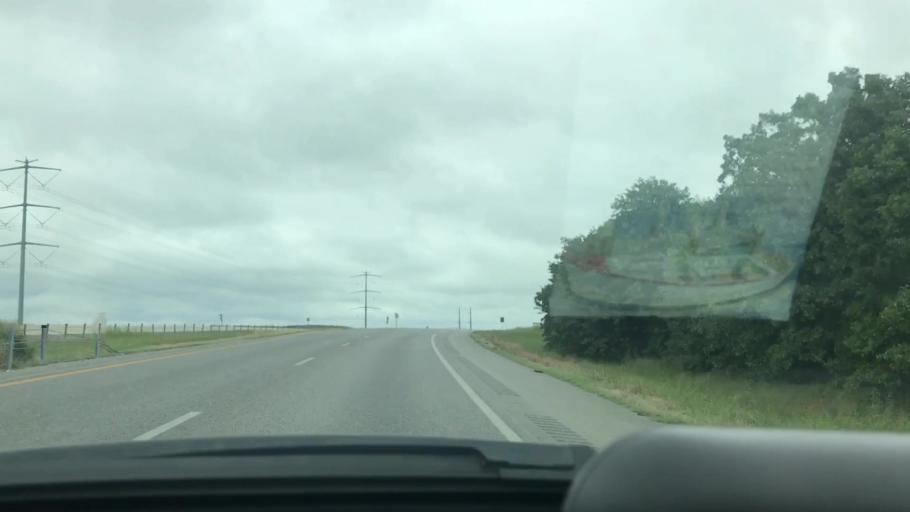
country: US
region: Oklahoma
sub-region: Pittsburg County
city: McAlester
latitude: 34.6758
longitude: -95.9343
